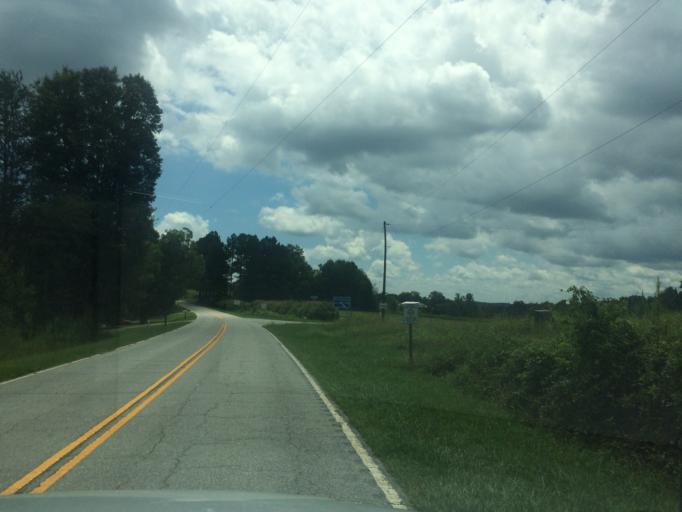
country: US
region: South Carolina
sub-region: Spartanburg County
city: Landrum
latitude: 35.1887
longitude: -82.0480
